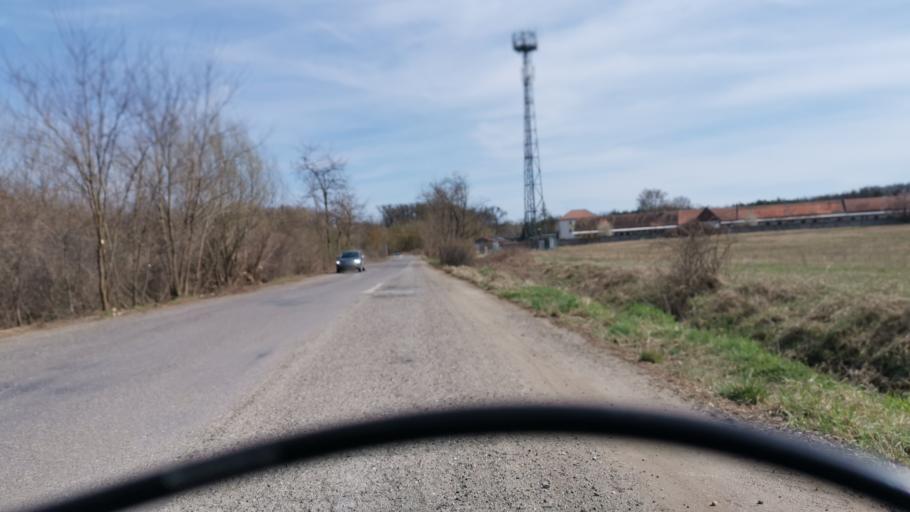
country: CZ
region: South Moravian
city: Tvrdonice
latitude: 48.7250
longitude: 17.0406
